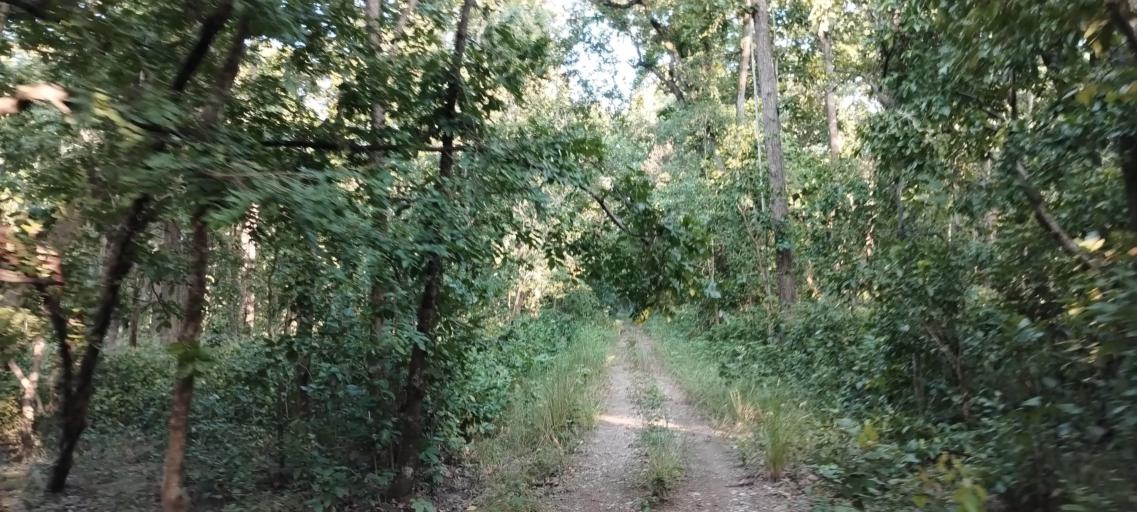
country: NP
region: Far Western
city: Tikapur
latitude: 28.4873
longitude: 81.2607
